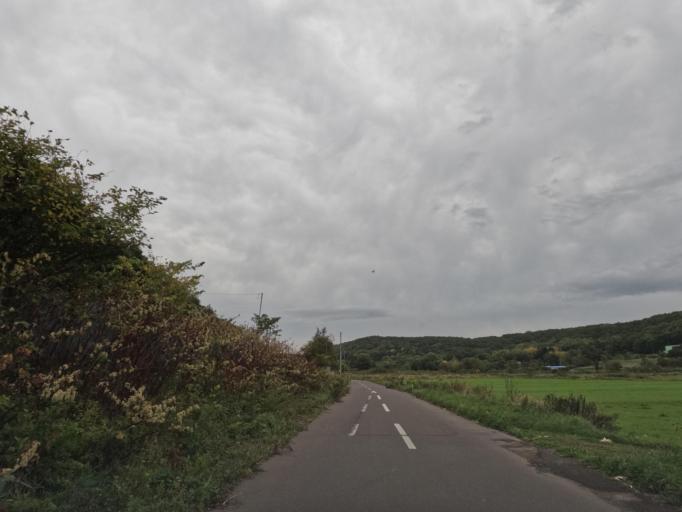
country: JP
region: Hokkaido
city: Date
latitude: 42.3997
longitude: 140.9146
